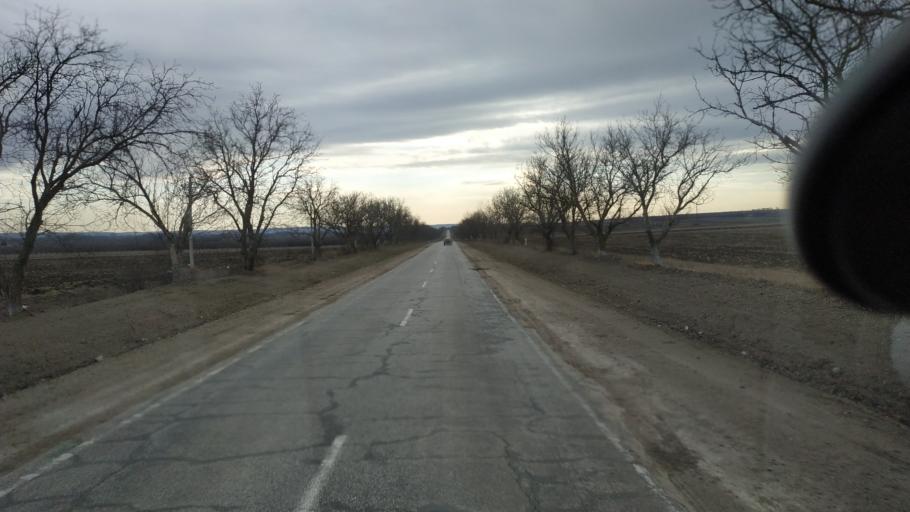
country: MD
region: Criuleni
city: Criuleni
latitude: 47.1939
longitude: 29.1486
